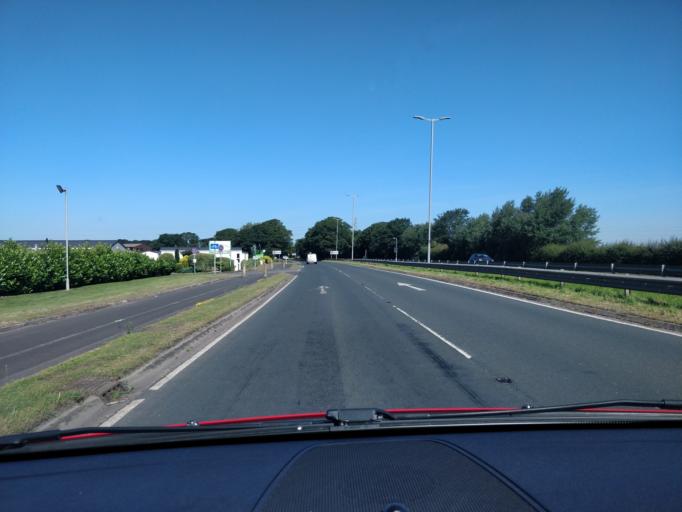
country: GB
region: England
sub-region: Lancashire
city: Banks
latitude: 53.6671
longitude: -2.9001
